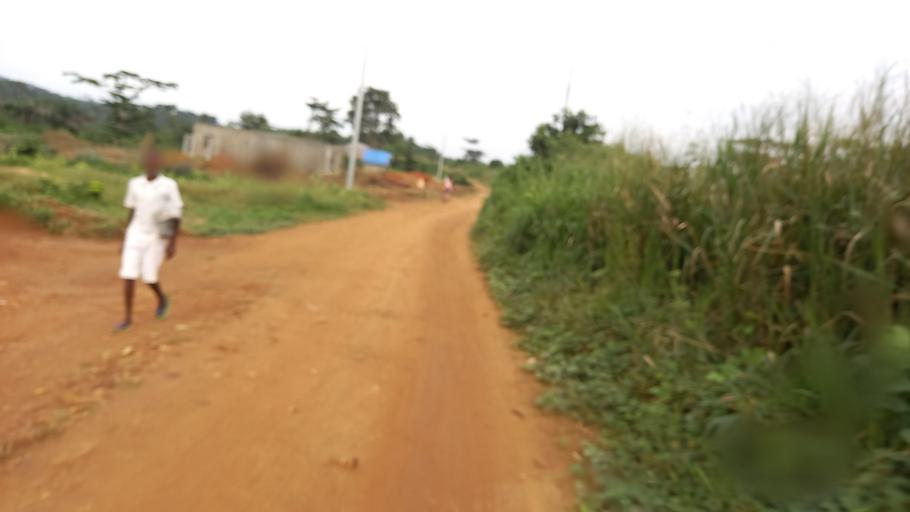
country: SL
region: Eastern Province
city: Kailahun
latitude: 8.2759
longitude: -10.5850
